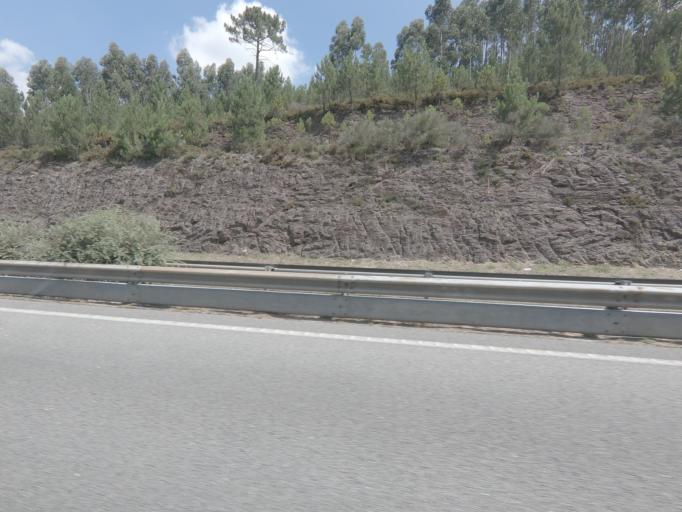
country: PT
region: Porto
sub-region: Paredes
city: Recarei
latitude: 41.1683
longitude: -8.4061
